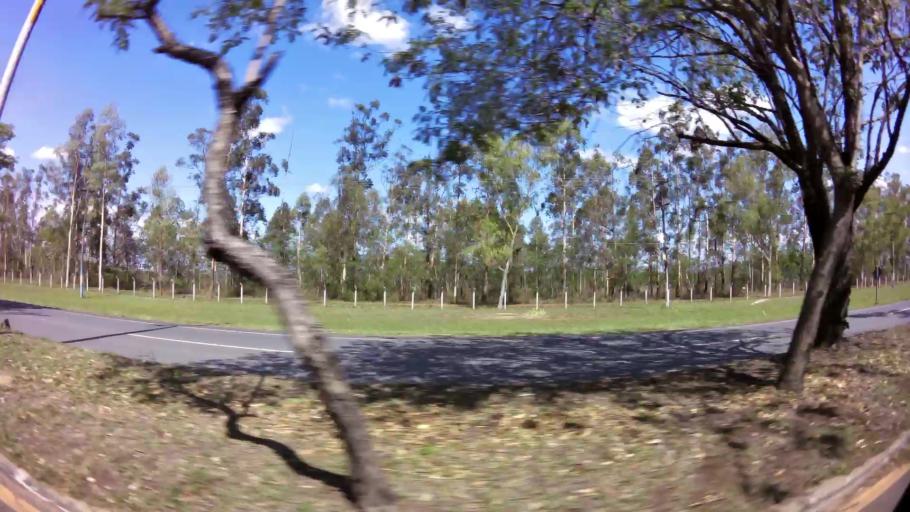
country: PY
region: Central
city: Fernando de la Mora
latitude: -25.2649
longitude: -57.5347
